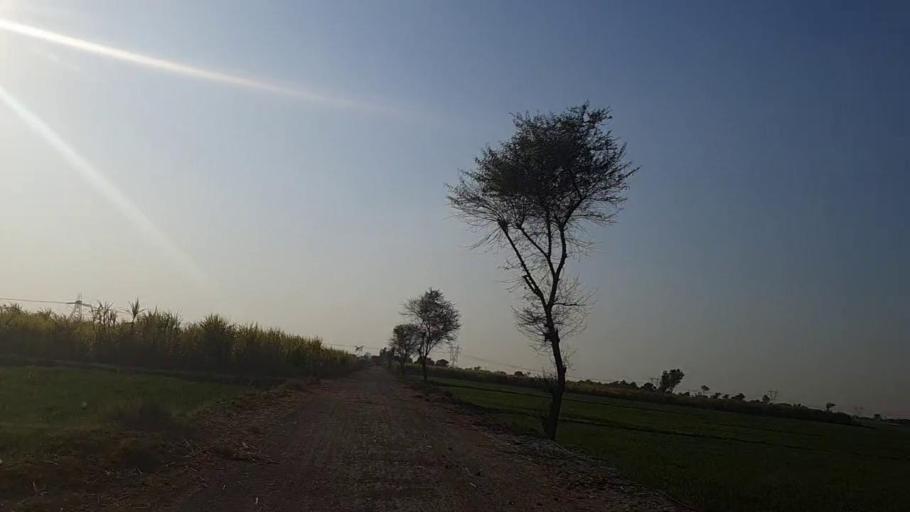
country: PK
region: Sindh
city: Sakrand
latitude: 26.3111
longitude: 68.1554
